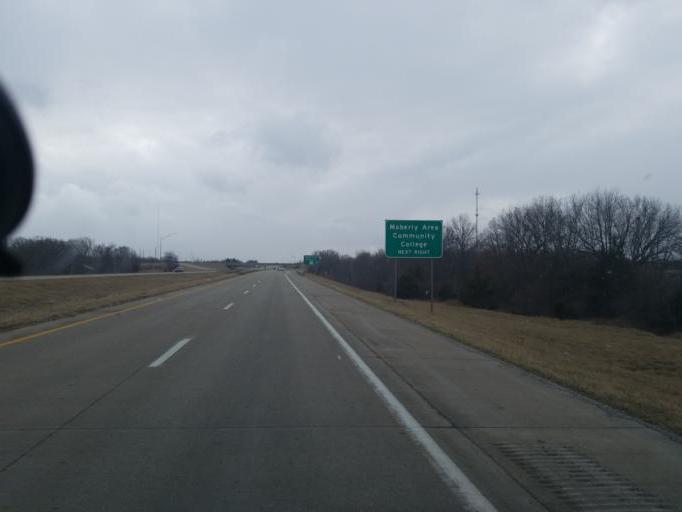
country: US
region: Missouri
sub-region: Randolph County
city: Moberly
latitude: 39.4225
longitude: -92.4121
